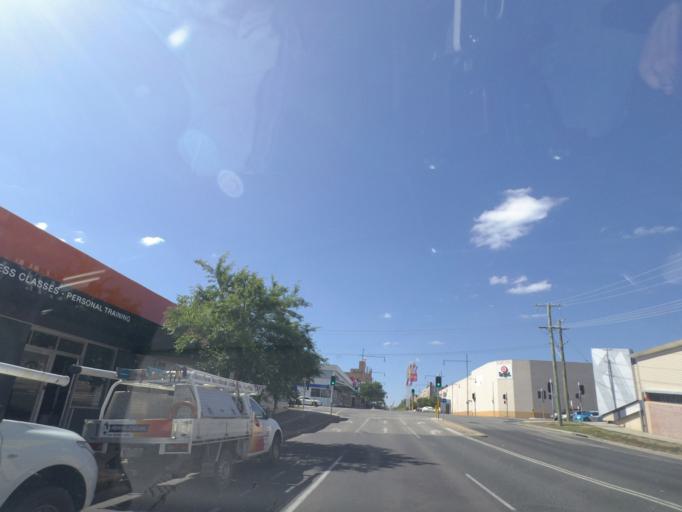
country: AU
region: New South Wales
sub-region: Albury Municipality
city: South Albury
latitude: -36.0832
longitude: 146.9151
